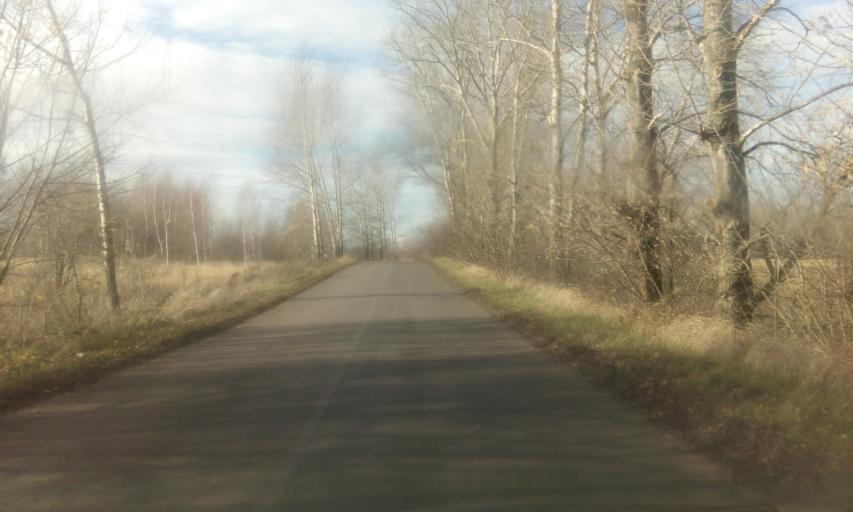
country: RU
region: Tula
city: Dubovka
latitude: 53.9578
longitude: 38.0556
